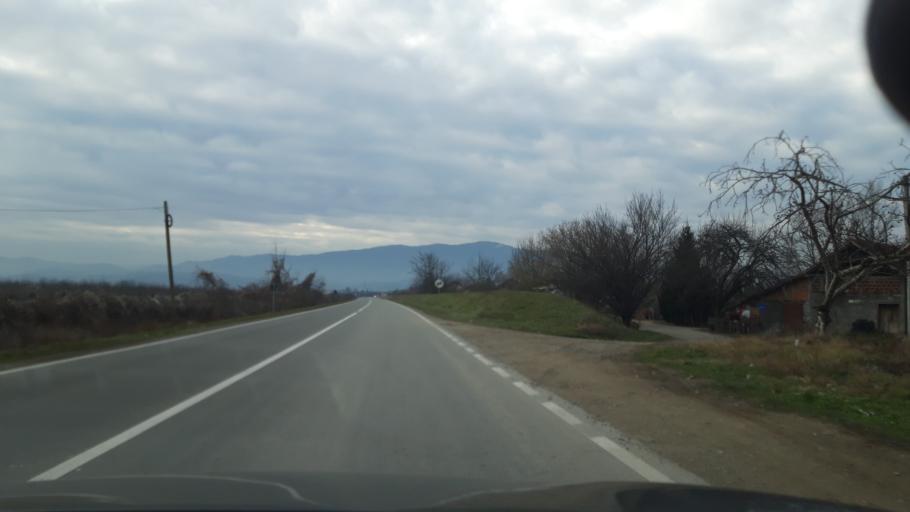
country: RS
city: Lipnicki Sor
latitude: 44.5597
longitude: 19.1993
